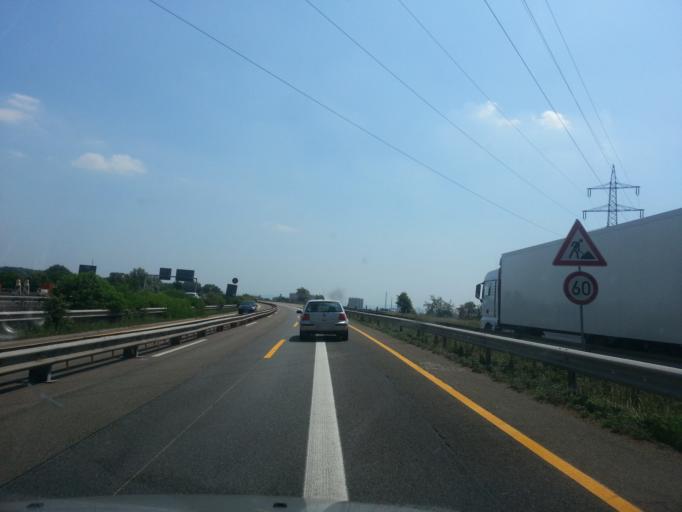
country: DE
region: Rheinland-Pfalz
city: Frankenthal
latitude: 49.5468
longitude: 8.3964
